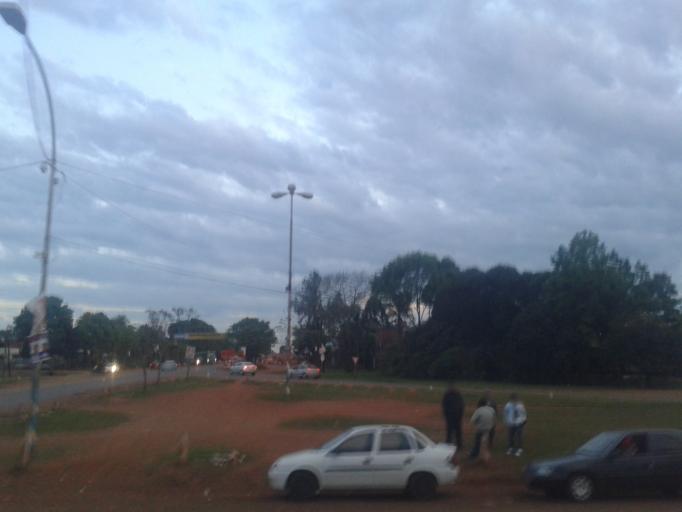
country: AR
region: Misiones
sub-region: Departamento de Candelaria
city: Candelaria
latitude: -27.4709
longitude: -55.7458
